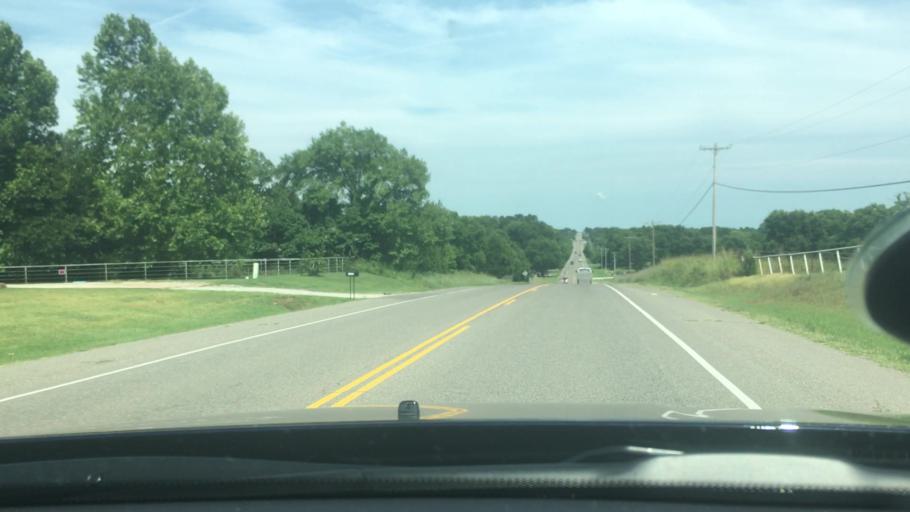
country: US
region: Oklahoma
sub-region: Pottawatomie County
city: Shawnee
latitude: 35.3331
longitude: -96.8212
